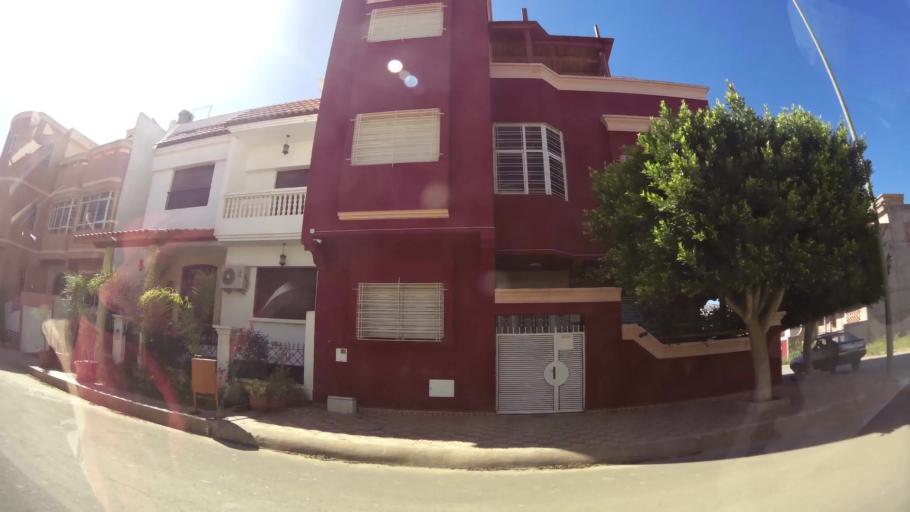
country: MA
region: Oriental
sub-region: Berkane-Taourirt
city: Berkane
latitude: 34.9447
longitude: -2.3340
